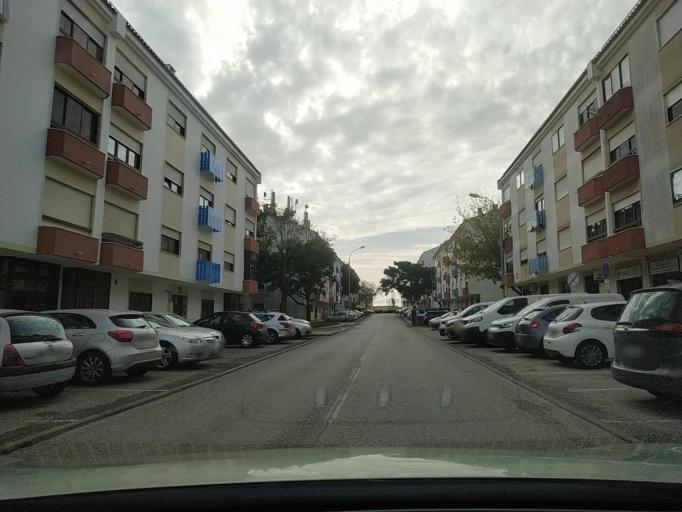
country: PT
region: Lisbon
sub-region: Odivelas
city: Famoes
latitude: 38.7802
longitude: -9.2339
